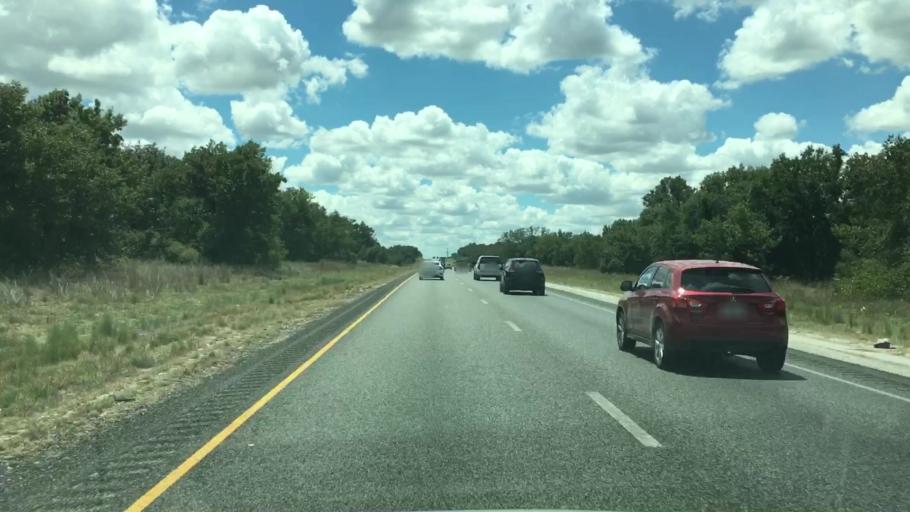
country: US
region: Texas
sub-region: Bexar County
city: Elmendorf
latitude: 29.1967
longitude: -98.4213
